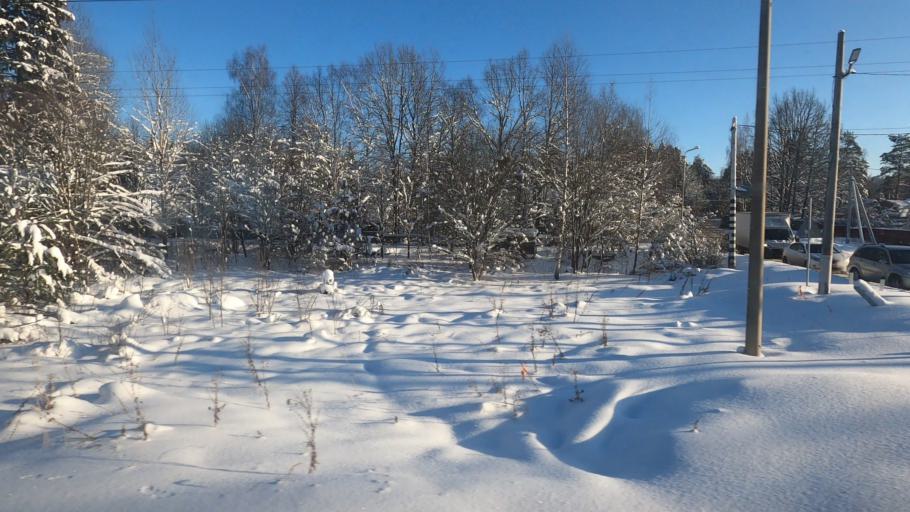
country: RU
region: Moskovskaya
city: Novo-Nikol'skoye
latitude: 56.5470
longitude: 37.5601
